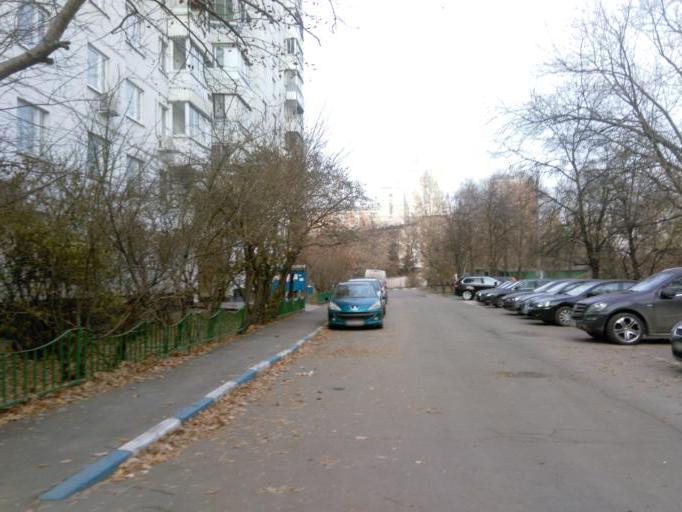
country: RU
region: Moscow
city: Troparevo
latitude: 55.6541
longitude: 37.5134
